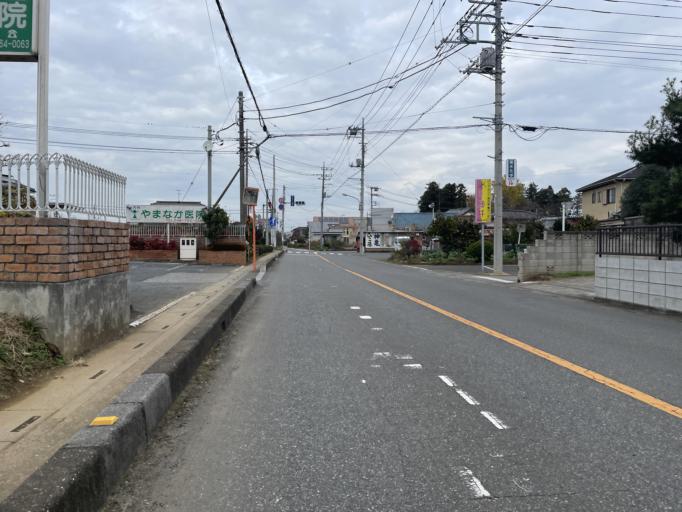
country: JP
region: Saitama
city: Shiraoka
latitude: 36.0052
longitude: 139.6615
